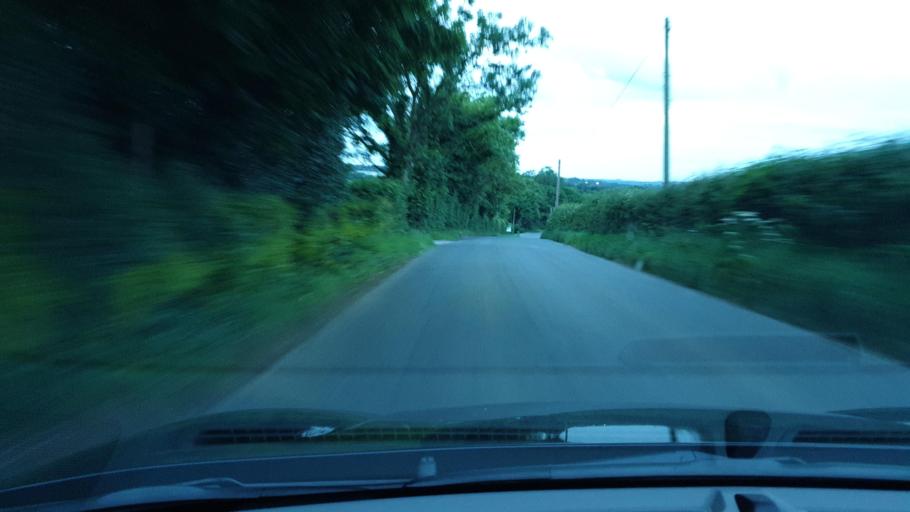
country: IE
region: Leinster
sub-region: An Mhi
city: Ashbourne
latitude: 53.5668
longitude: -6.4141
